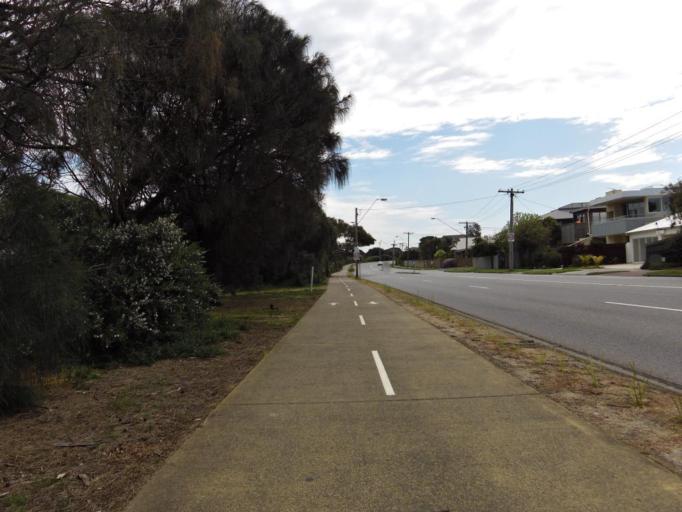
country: AU
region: Victoria
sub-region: Bayside
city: Black Rock
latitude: -37.9720
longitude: 145.0131
